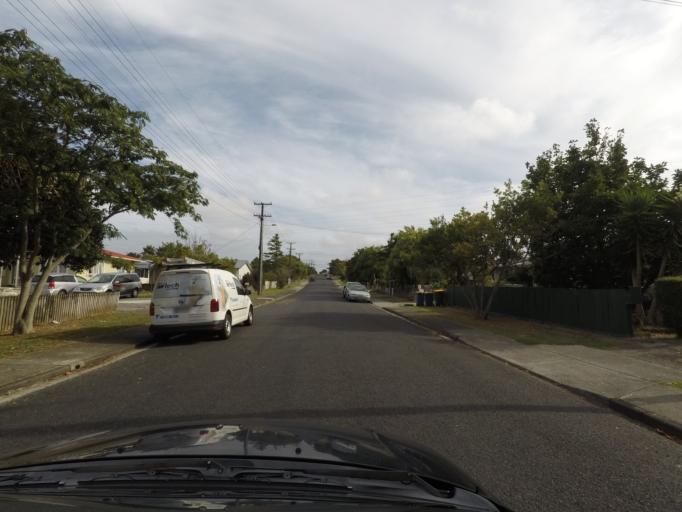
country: NZ
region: Auckland
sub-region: Auckland
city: Rosebank
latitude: -36.8921
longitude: 174.6676
